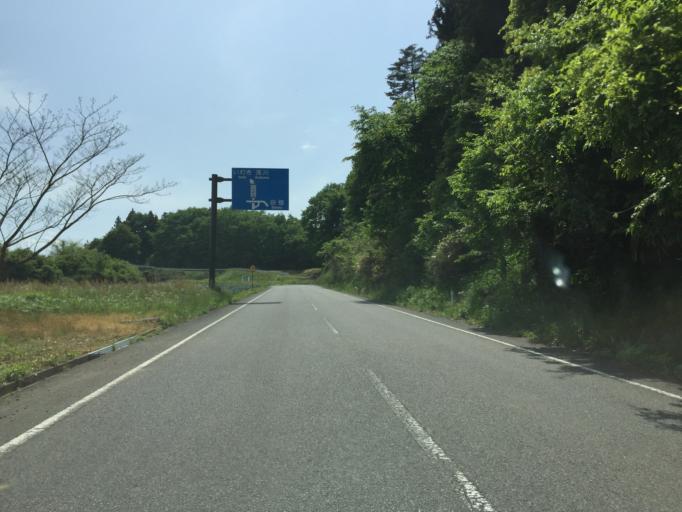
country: JP
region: Fukushima
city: Ishikawa
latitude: 37.1755
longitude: 140.5057
